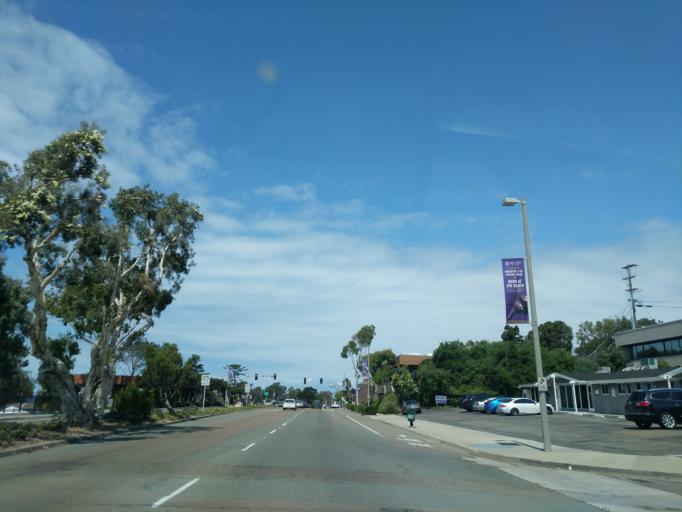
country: US
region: California
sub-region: San Diego County
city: Del Mar
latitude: 32.9522
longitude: -117.2625
